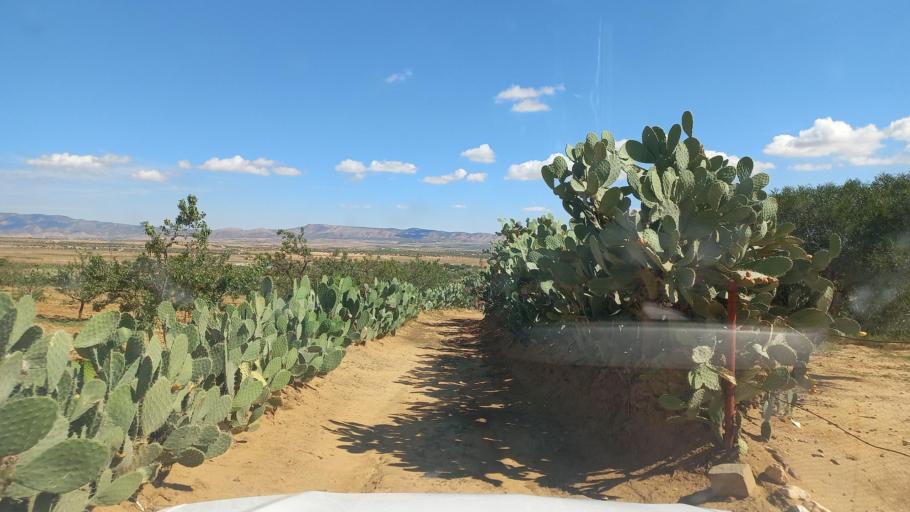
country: TN
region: Al Qasrayn
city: Sbiba
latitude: 35.3611
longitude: 9.0183
